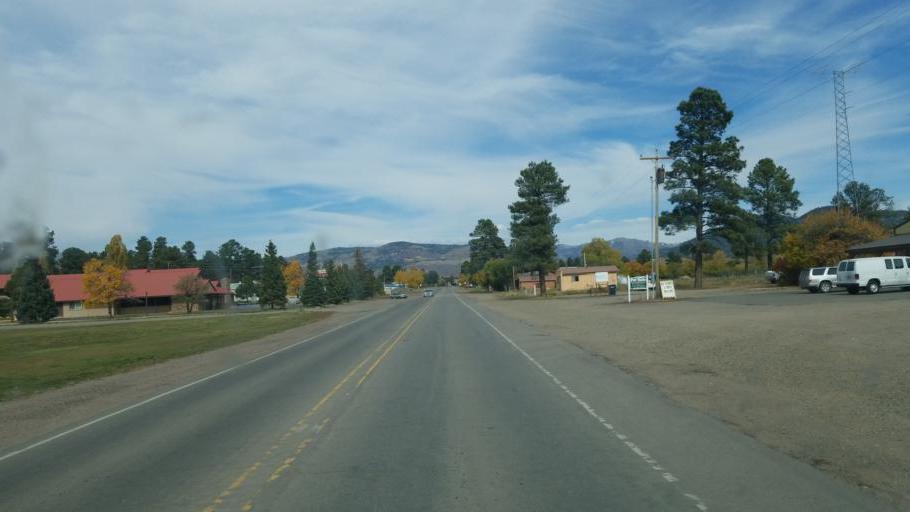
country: US
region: New Mexico
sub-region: Rio Arriba County
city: Chama
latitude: 36.8913
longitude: -106.5828
